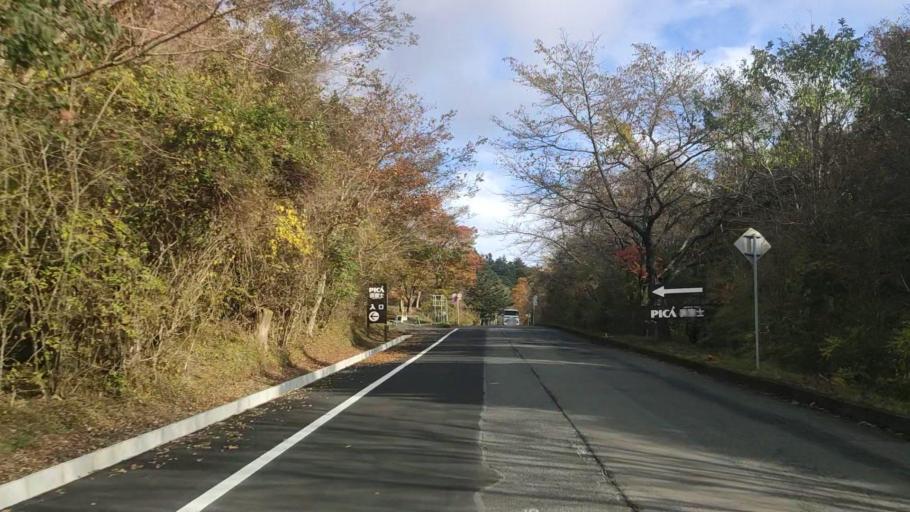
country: JP
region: Shizuoka
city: Fujinomiya
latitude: 35.2976
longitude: 138.6997
